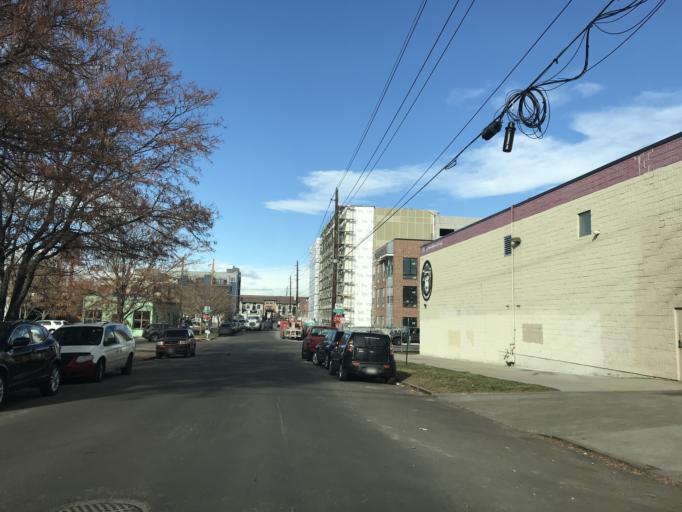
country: US
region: Colorado
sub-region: Denver County
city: Denver
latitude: 39.7638
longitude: -104.9776
